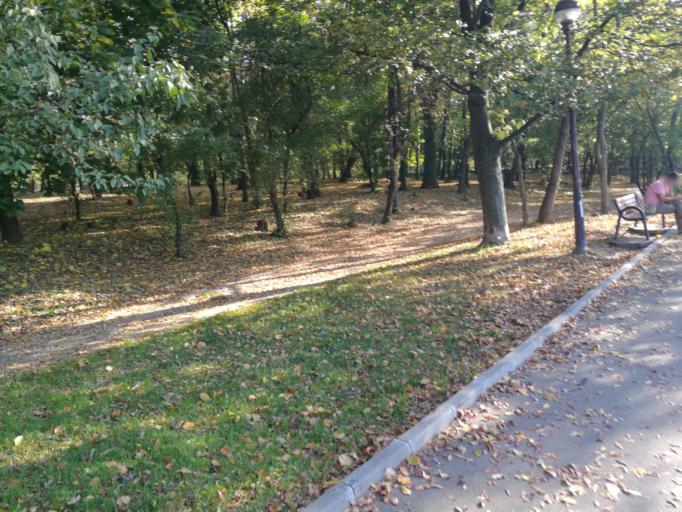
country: RO
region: Bucuresti
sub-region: Municipiul Bucuresti
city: Bucharest
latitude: 44.4849
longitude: 26.0843
